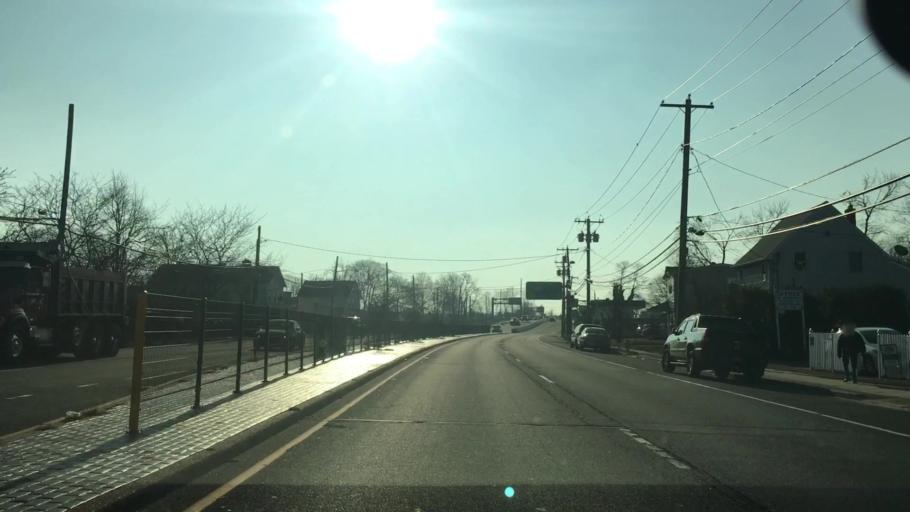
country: US
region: New York
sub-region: Suffolk County
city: North Amityville
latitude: 40.6899
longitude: -73.4208
